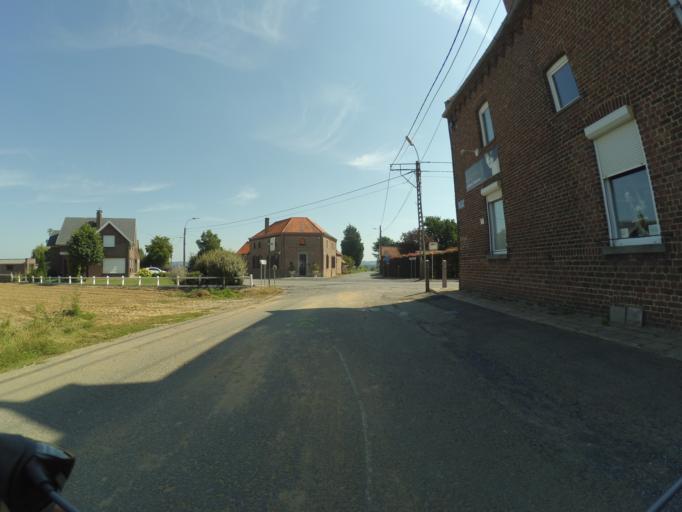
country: BE
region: Flanders
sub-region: Provincie Oost-Vlaanderen
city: Ronse
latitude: 50.7509
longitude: 3.5445
